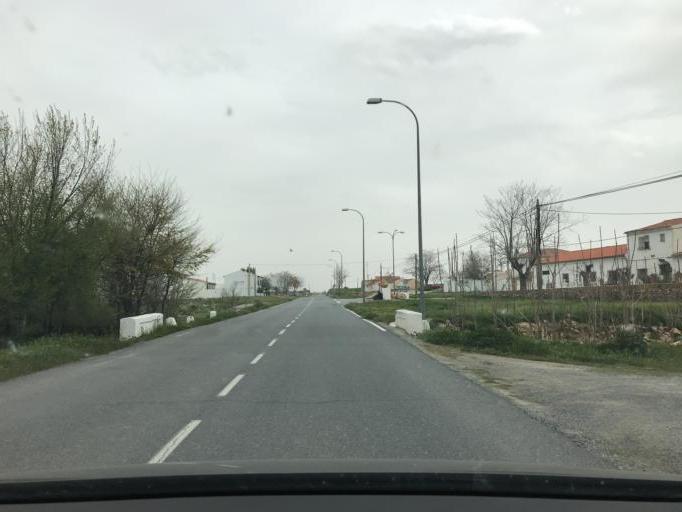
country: ES
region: Andalusia
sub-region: Provincia de Granada
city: Gor
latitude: 37.3739
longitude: -3.0644
